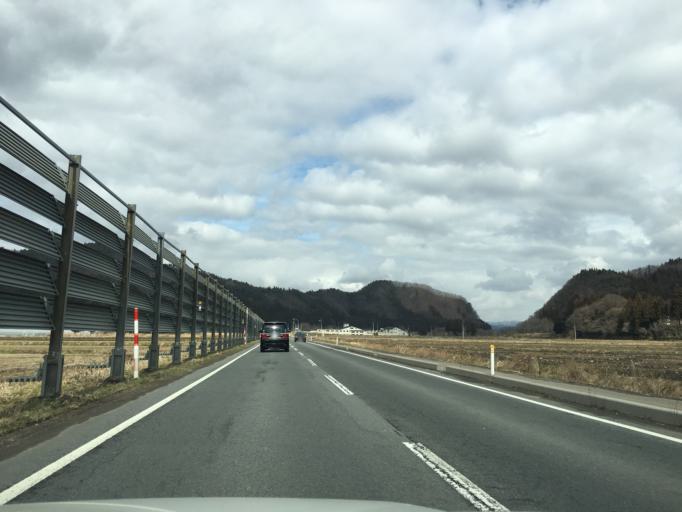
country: JP
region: Akita
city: Hanawa
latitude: 40.2380
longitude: 140.7371
